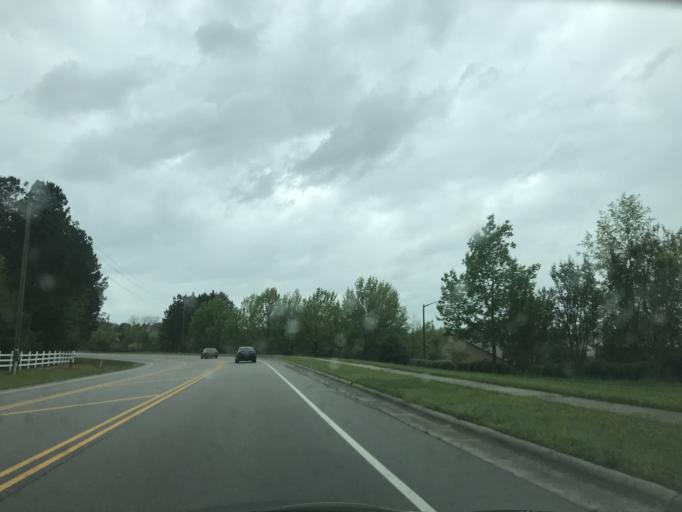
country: US
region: North Carolina
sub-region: Wake County
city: Knightdale
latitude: 35.8079
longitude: -78.4814
